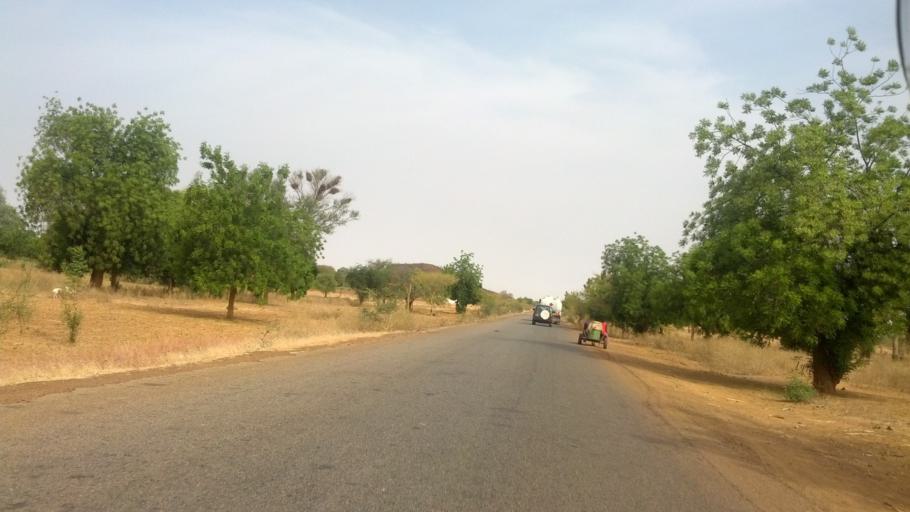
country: BF
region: Centre-Nord
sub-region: Province du Sanmatenga
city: Kaya
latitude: 12.9164
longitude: -1.0779
